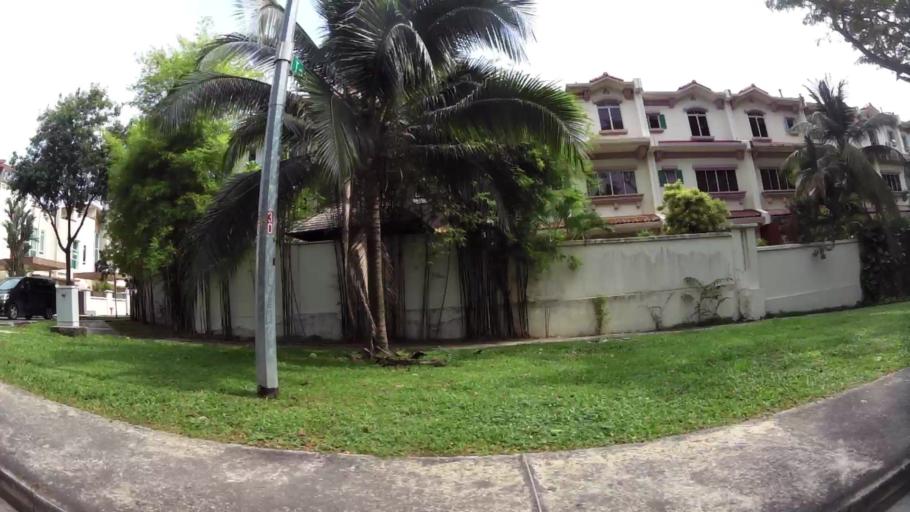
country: SG
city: Singapore
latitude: 1.3629
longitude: 103.9709
